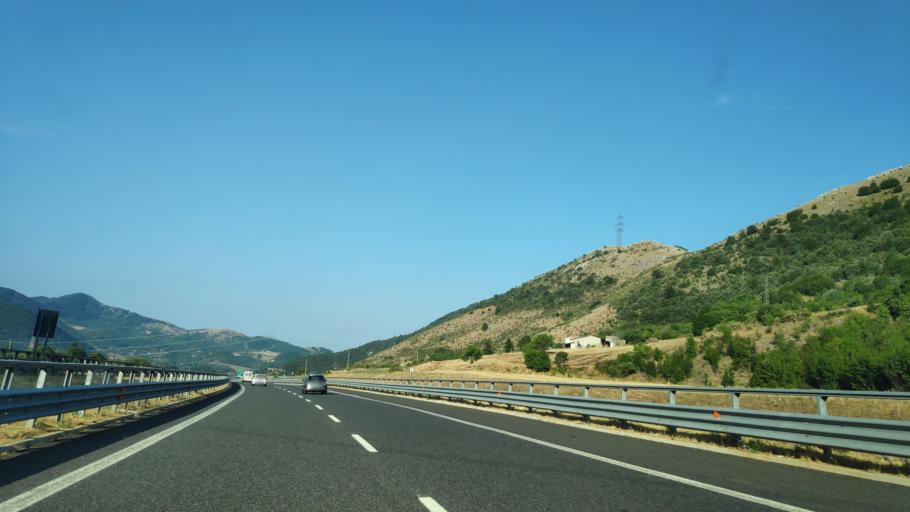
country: IT
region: Calabria
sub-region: Provincia di Cosenza
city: Mormanno
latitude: 39.8882
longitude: 16.0288
